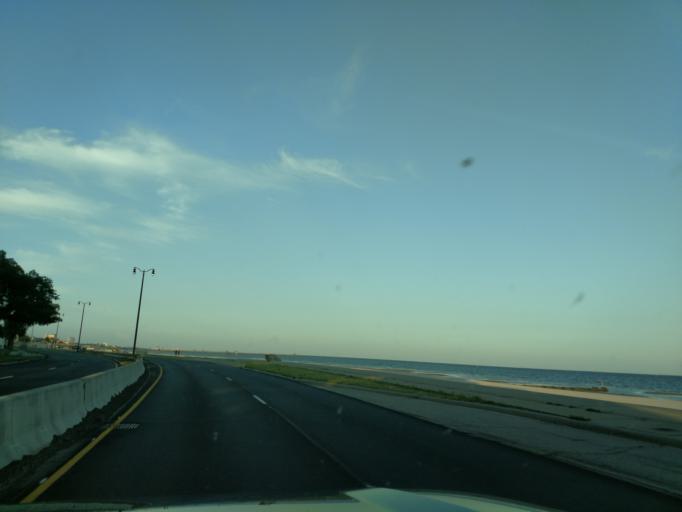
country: US
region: Mississippi
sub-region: Harrison County
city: Gulfport
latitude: 30.3750
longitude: -89.0565
